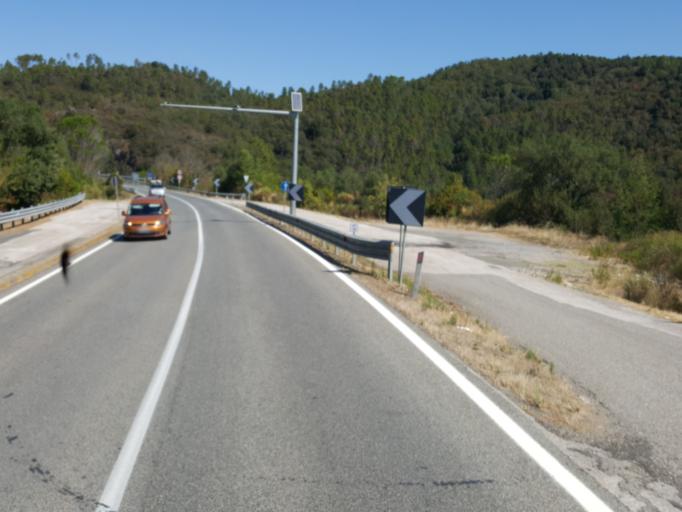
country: IT
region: Tuscany
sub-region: Provincia di Grosseto
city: Civitella Marittima
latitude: 43.0124
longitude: 11.2881
